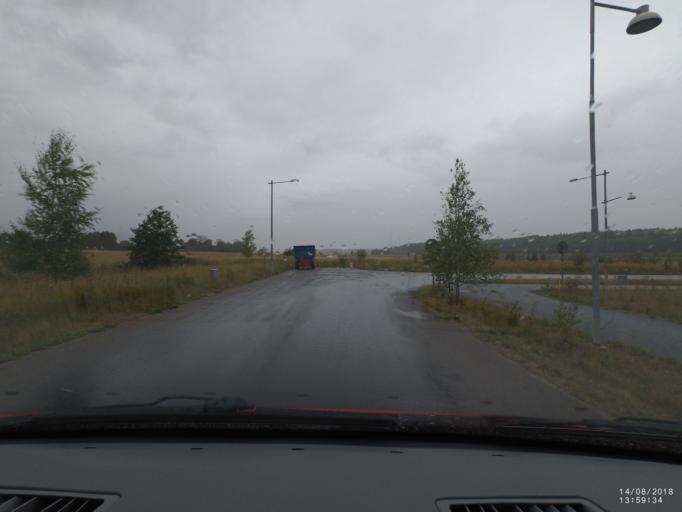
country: SE
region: Soedermanland
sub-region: Nykopings Kommun
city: Nykoping
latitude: 58.7533
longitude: 16.9705
